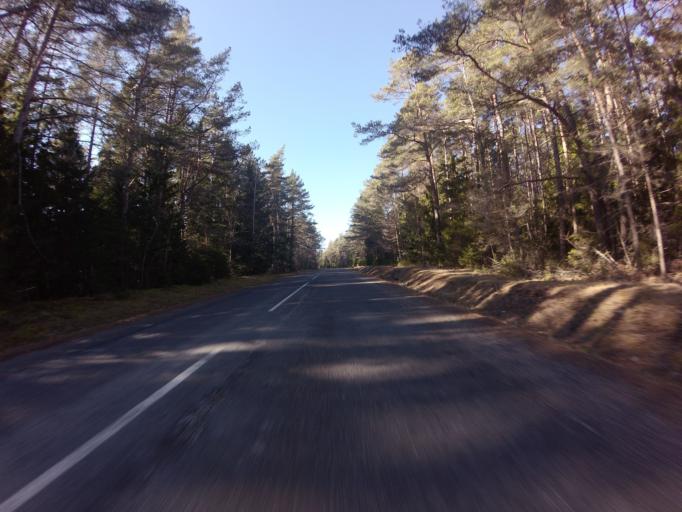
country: EE
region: Saare
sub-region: Kuressaare linn
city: Kuressaare
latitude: 58.5942
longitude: 22.6012
